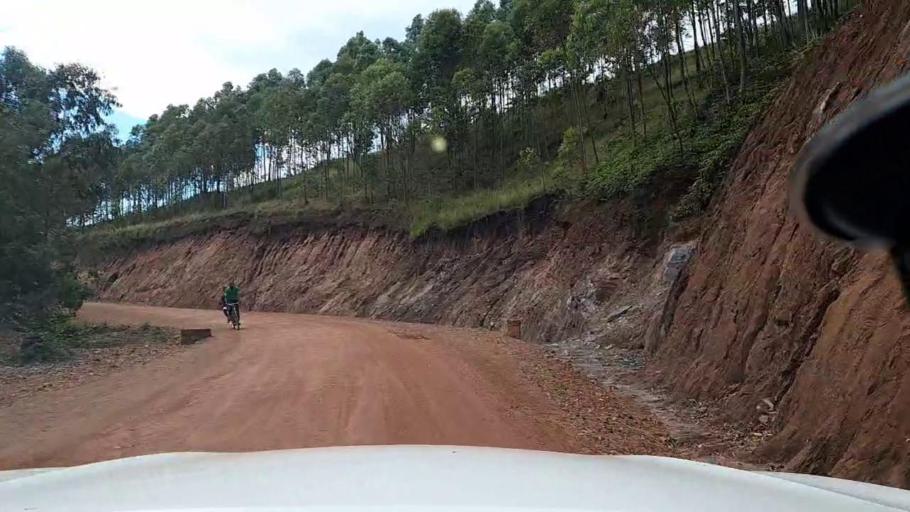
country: RW
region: Kigali
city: Kigali
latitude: -1.7604
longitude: 29.8427
